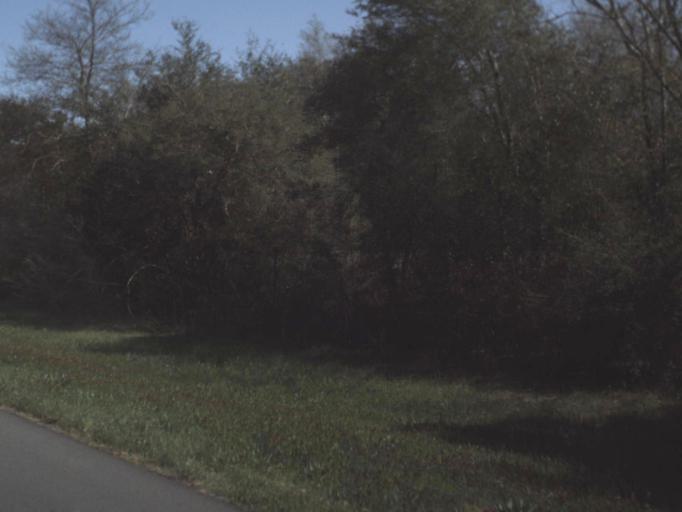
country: US
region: Florida
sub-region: Walton County
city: DeFuniak Springs
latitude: 30.7462
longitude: -86.2224
